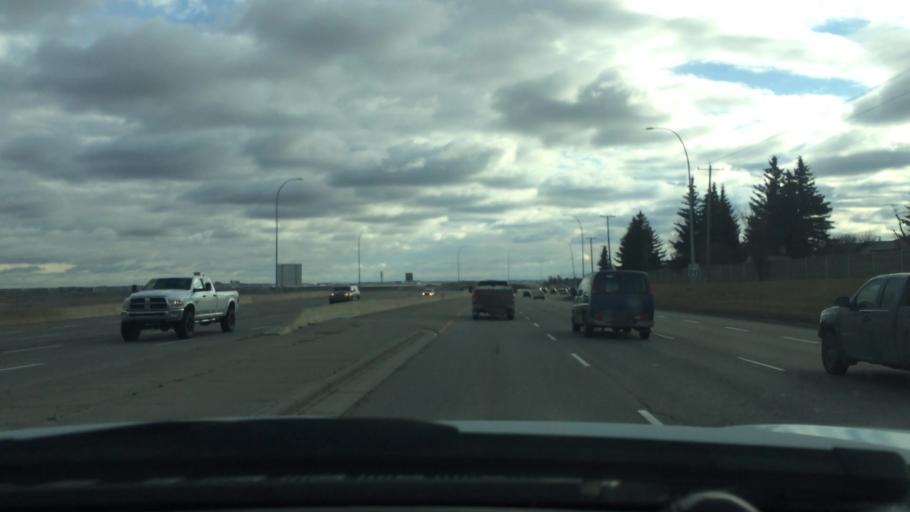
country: CA
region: Alberta
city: Calgary
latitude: 51.1372
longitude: -114.0786
